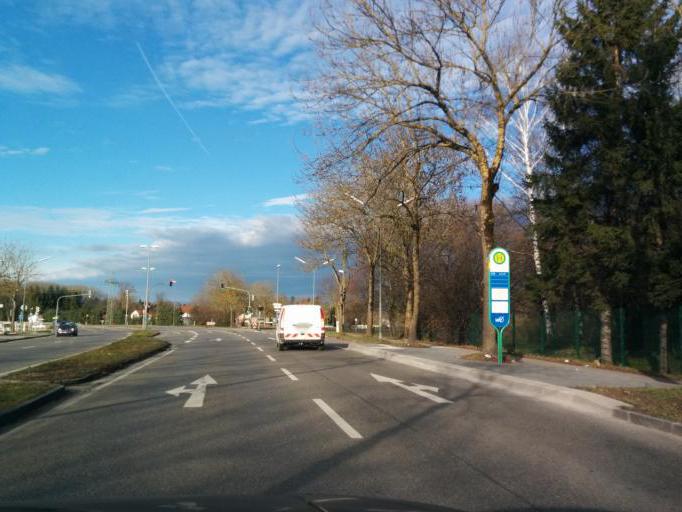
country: DE
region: Bavaria
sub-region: Upper Bavaria
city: Karlsfeld
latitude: 48.2278
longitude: 11.4640
